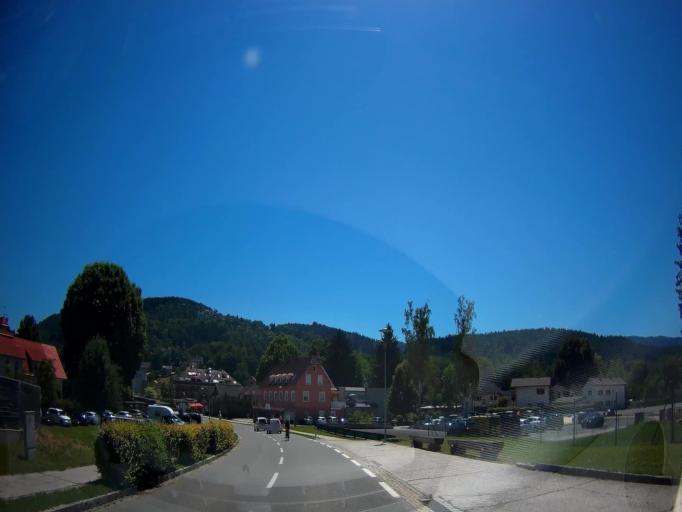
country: AT
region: Carinthia
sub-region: Politischer Bezirk Klagenfurt Land
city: Keutschach am See
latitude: 46.6079
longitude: 14.1793
